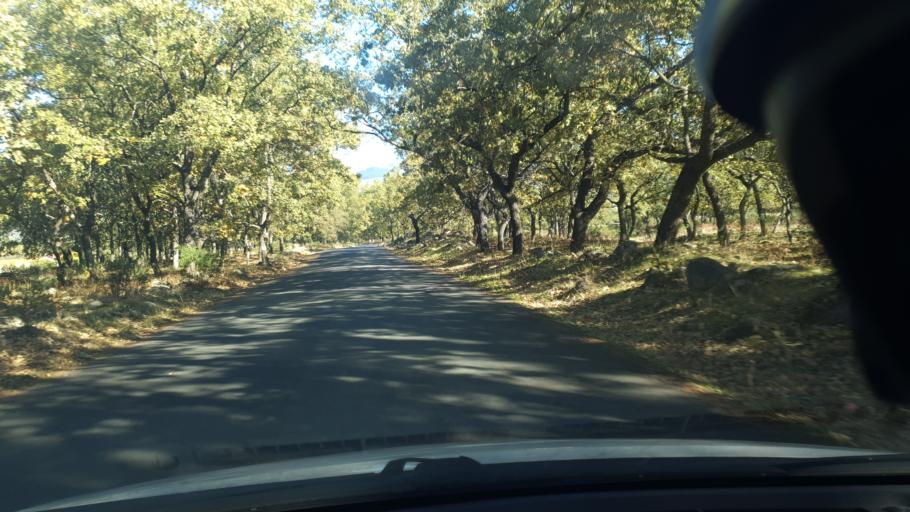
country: ES
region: Castille and Leon
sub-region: Provincia de Avila
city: Candeleda
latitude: 40.1373
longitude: -5.2607
